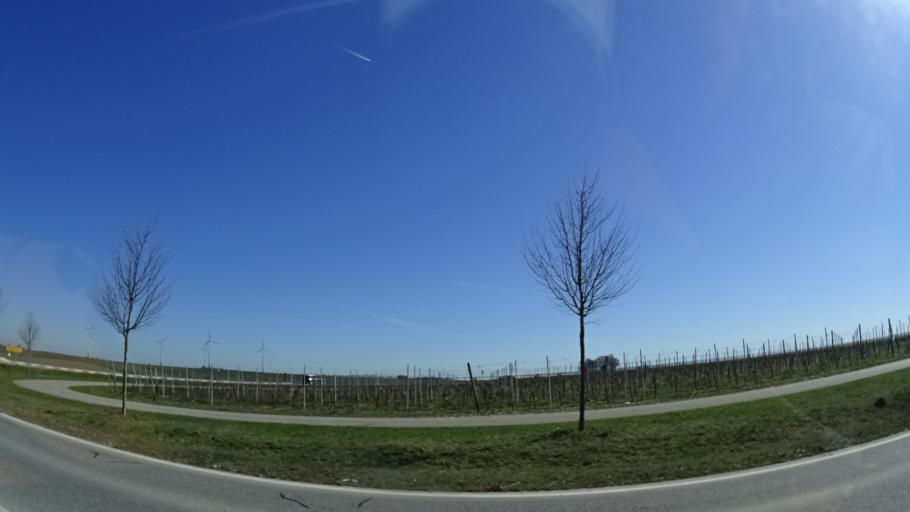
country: DE
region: Rheinland-Pfalz
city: Friesenheim
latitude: 49.8418
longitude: 8.2555
